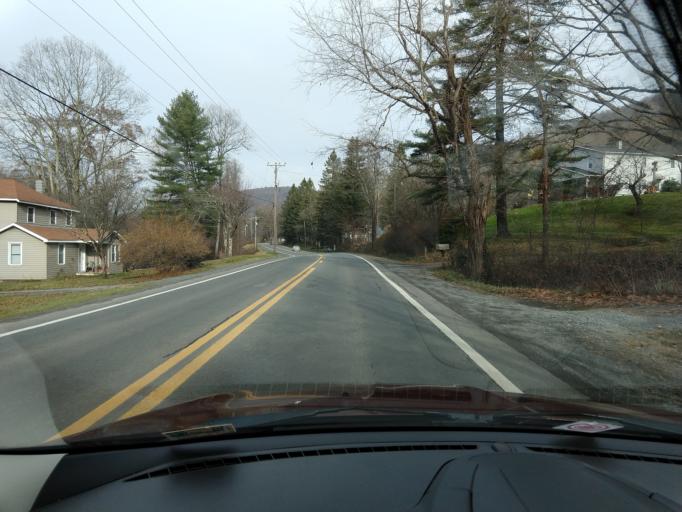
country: US
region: West Virginia
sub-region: Greenbrier County
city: Rainelle
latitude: 37.9748
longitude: -80.7094
